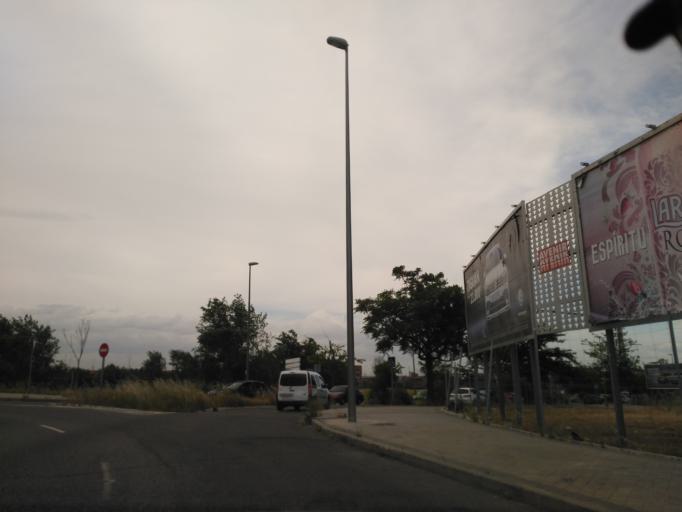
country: ES
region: Madrid
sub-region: Provincia de Madrid
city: Villaverde
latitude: 40.3403
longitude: -3.7175
